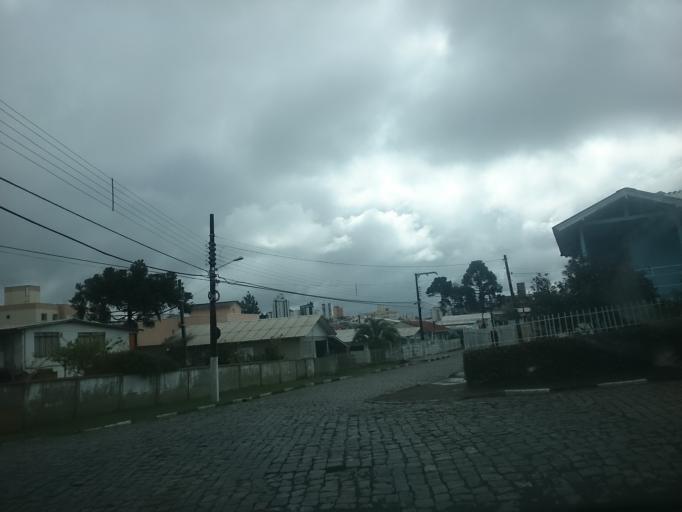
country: BR
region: Santa Catarina
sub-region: Lages
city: Lages
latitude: -27.8270
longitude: -50.3302
